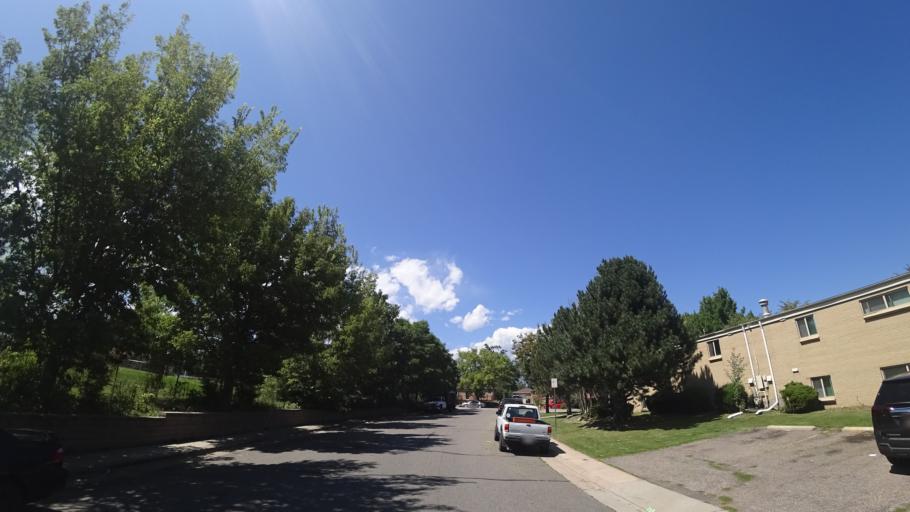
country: US
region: Colorado
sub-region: Arapahoe County
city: Littleton
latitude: 39.6107
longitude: -104.9905
